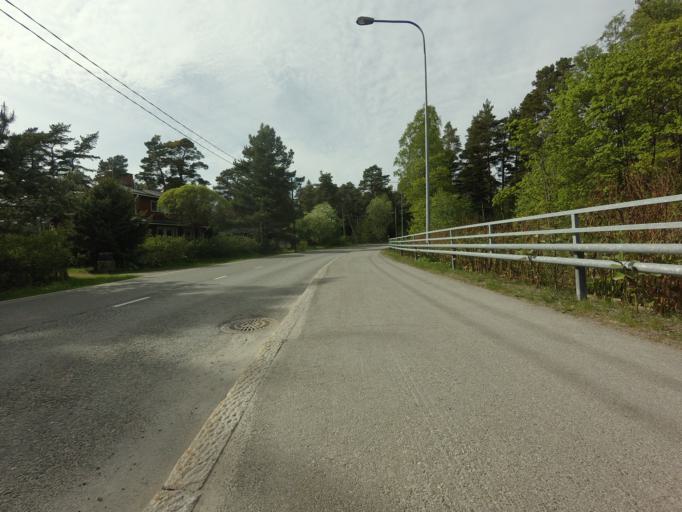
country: FI
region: Uusimaa
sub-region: Helsinki
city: Koukkuniemi
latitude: 60.1227
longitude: 24.7148
